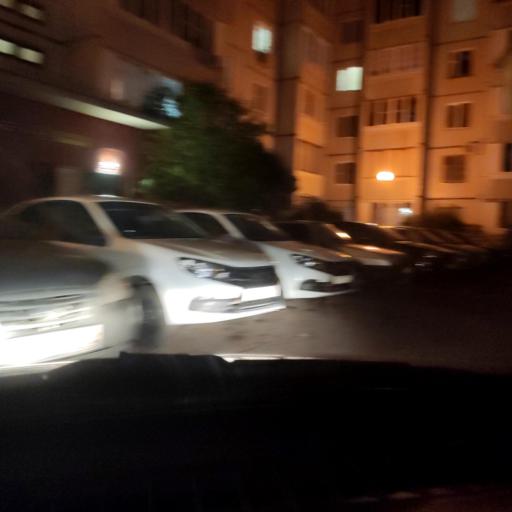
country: RU
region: Samara
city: Tol'yatti
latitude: 53.5437
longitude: 49.3235
